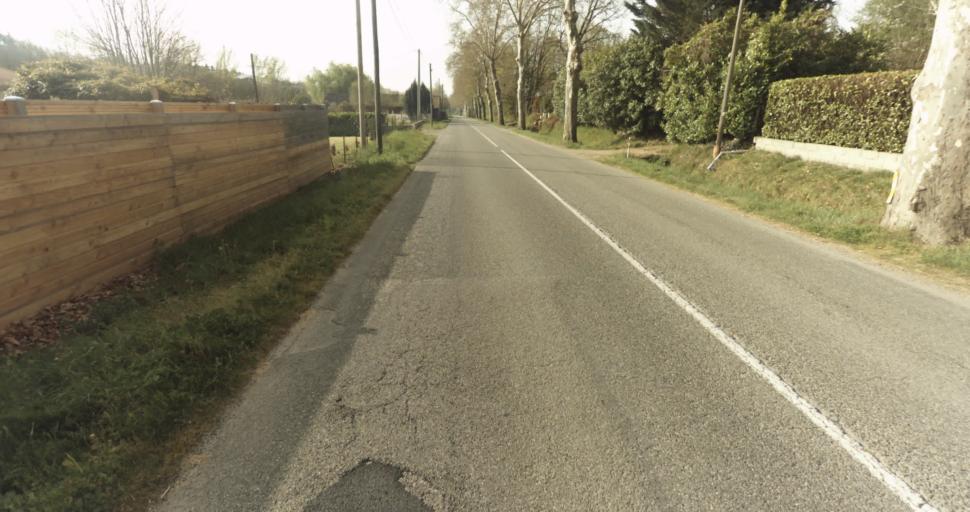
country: FR
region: Midi-Pyrenees
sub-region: Departement du Tarn-et-Garonne
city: Moissac
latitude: 44.1381
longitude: 1.1033
